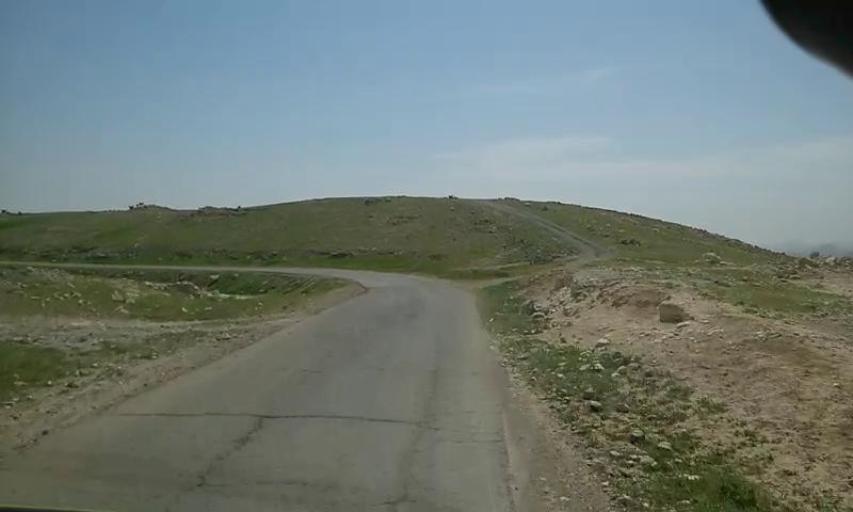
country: PS
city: `Arab ar Rashaydah
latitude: 31.5434
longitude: 35.2598
